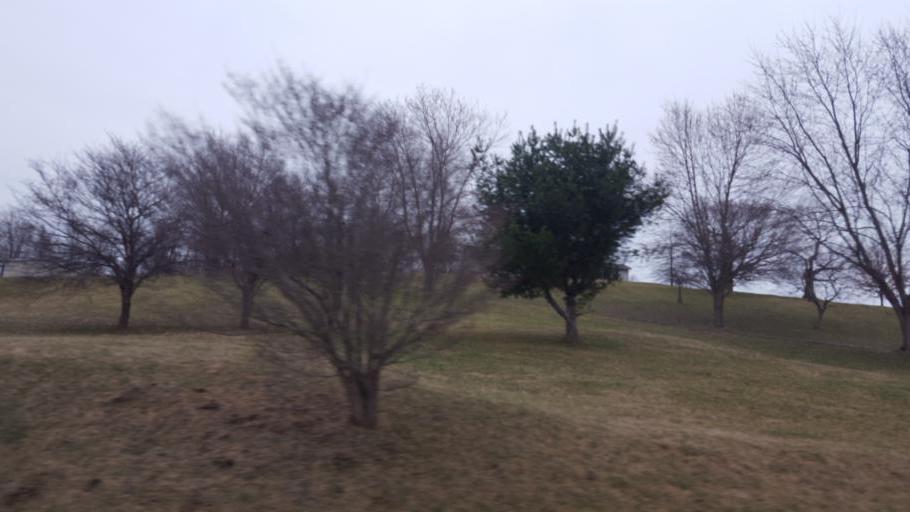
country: US
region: Ohio
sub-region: Knox County
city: Fredericktown
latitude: 40.5092
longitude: -82.5317
